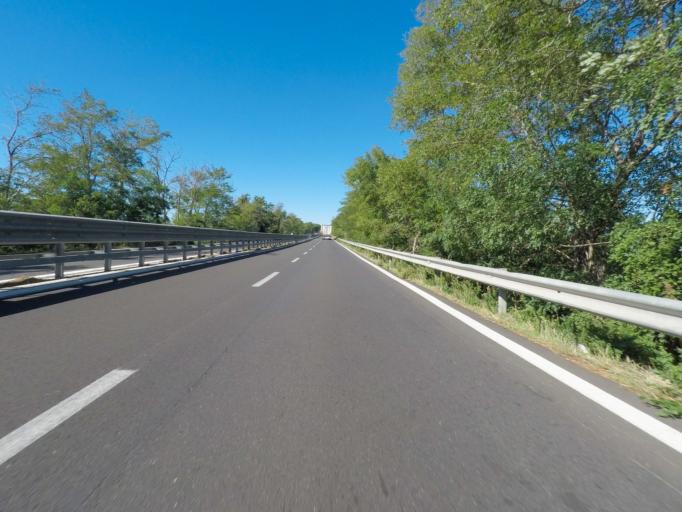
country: IT
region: Latium
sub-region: Provincia di Viterbo
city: Montalto di Castro
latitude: 42.3348
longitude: 11.6243
